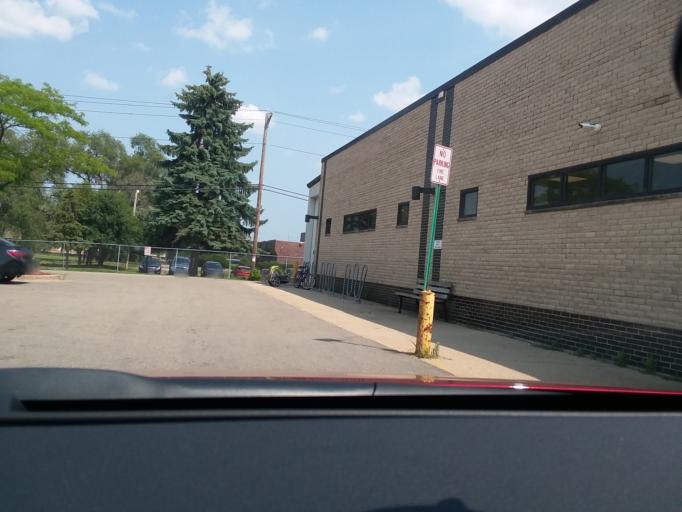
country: US
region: Wisconsin
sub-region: Dane County
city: Maple Bluff
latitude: 43.1136
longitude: -89.3608
